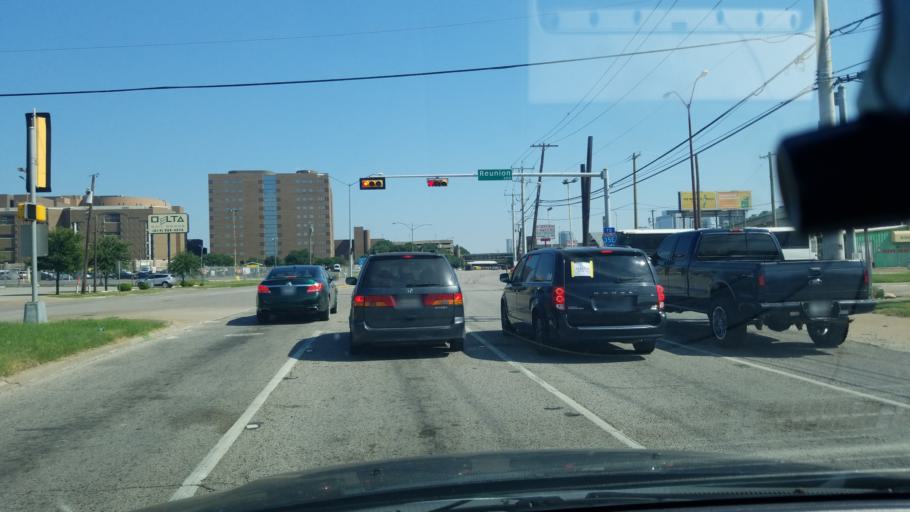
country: US
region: Texas
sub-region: Dallas County
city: Dallas
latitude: 32.7742
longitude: -96.8131
